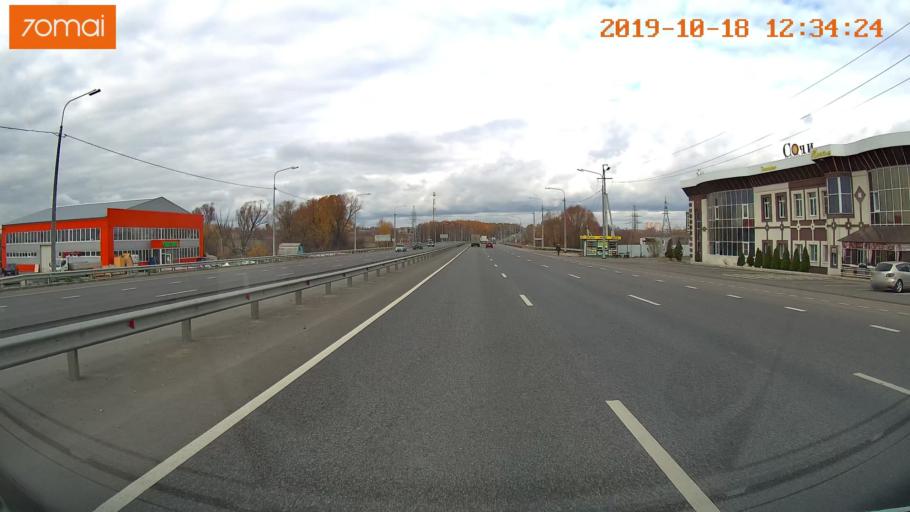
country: RU
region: Rjazan
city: Ryazan'
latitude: 54.6135
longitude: 39.6383
